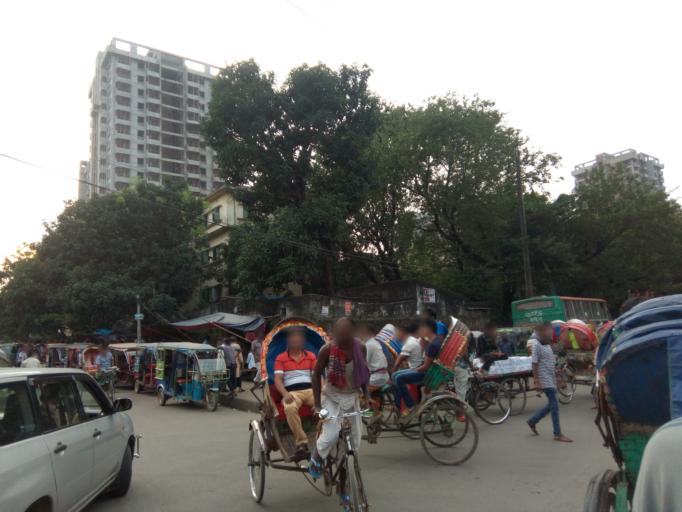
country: BD
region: Dhaka
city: Azimpur
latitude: 23.7240
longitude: 90.3872
